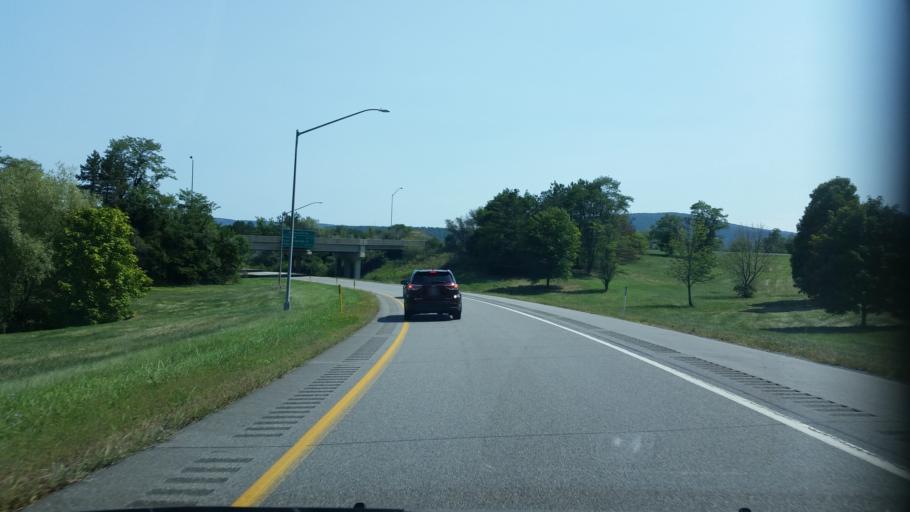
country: US
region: Pennsylvania
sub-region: Blair County
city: Duncansville
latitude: 40.4375
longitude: -78.4291
